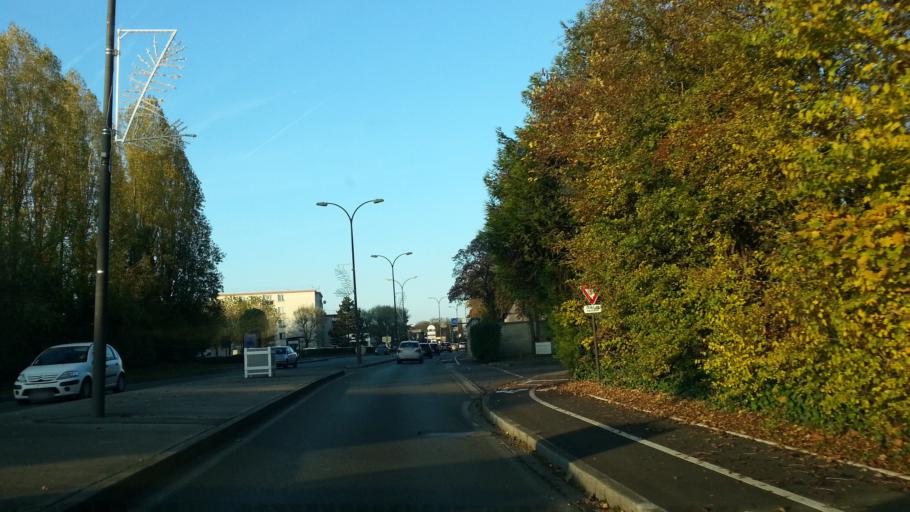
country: FR
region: Picardie
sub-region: Departement de l'Oise
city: Chantilly
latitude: 49.2004
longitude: 2.4606
